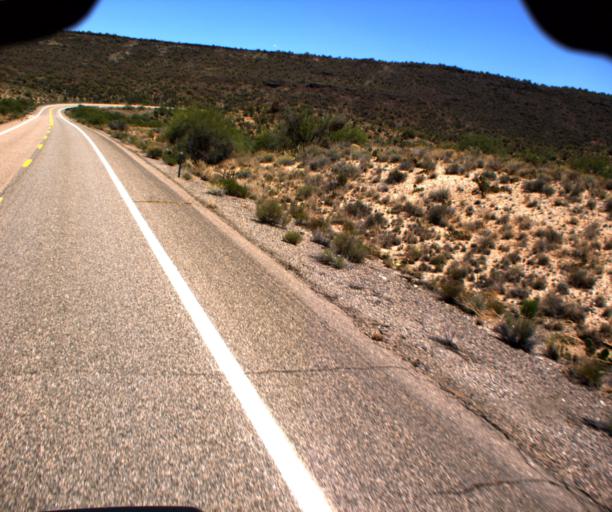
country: US
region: Arizona
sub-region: Yavapai County
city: Bagdad
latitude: 34.5167
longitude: -113.0816
